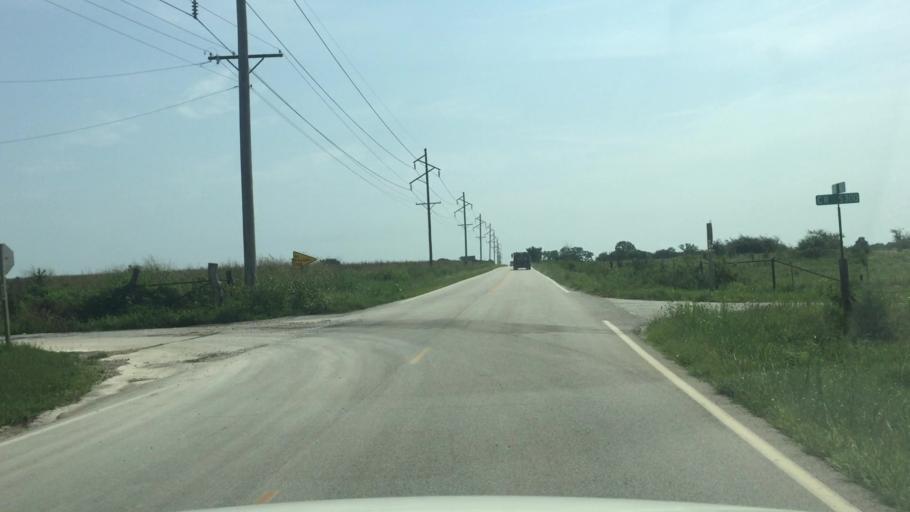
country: US
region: Kansas
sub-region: Montgomery County
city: Cherryvale
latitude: 37.2087
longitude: -95.5767
